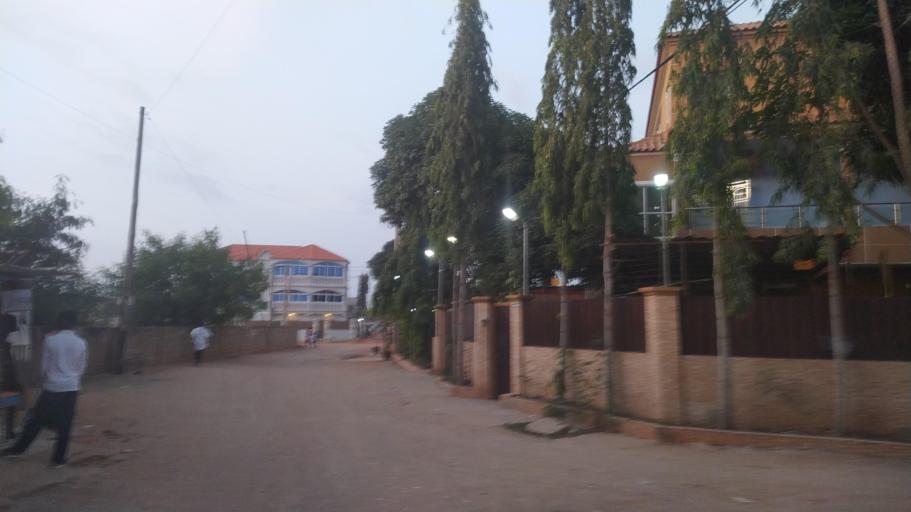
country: AO
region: Luanda
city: Luanda
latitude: -8.8963
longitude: 13.2049
